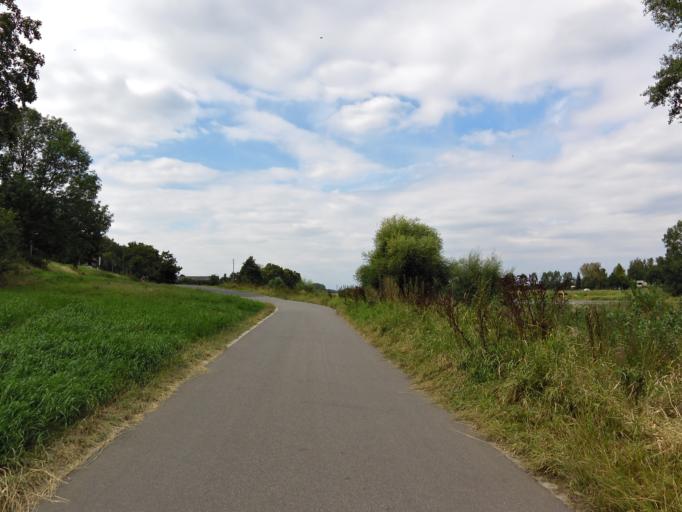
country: DE
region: Saxony
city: Coswig
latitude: 51.0955
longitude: 13.6026
